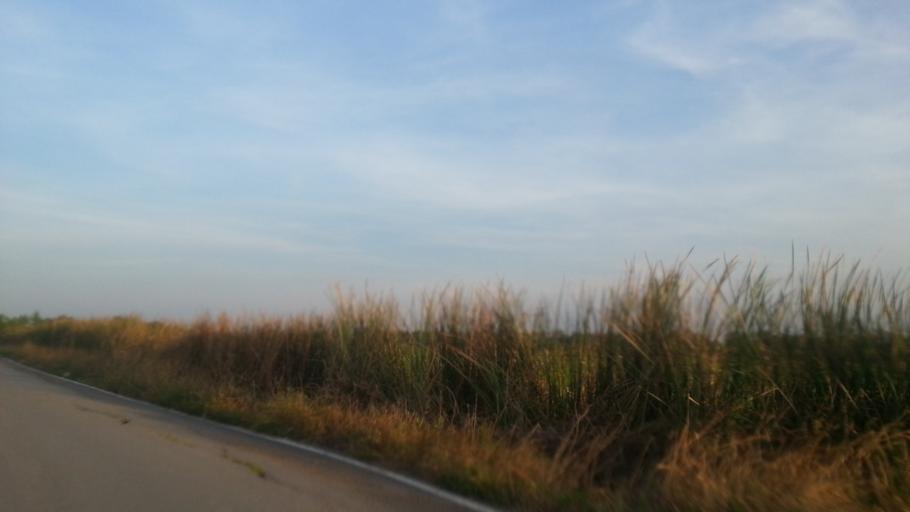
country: TH
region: Pathum Thani
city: Ban Lam Luk Ka
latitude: 14.0369
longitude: 100.8585
